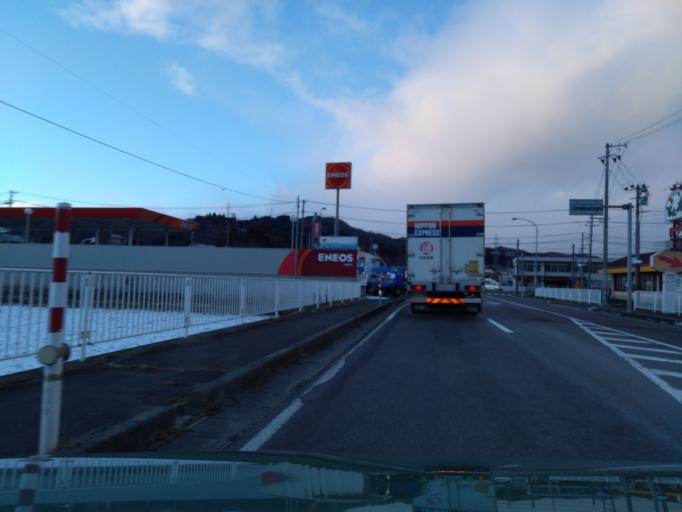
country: JP
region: Iwate
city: Shizukuishi
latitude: 39.6993
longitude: 141.0625
